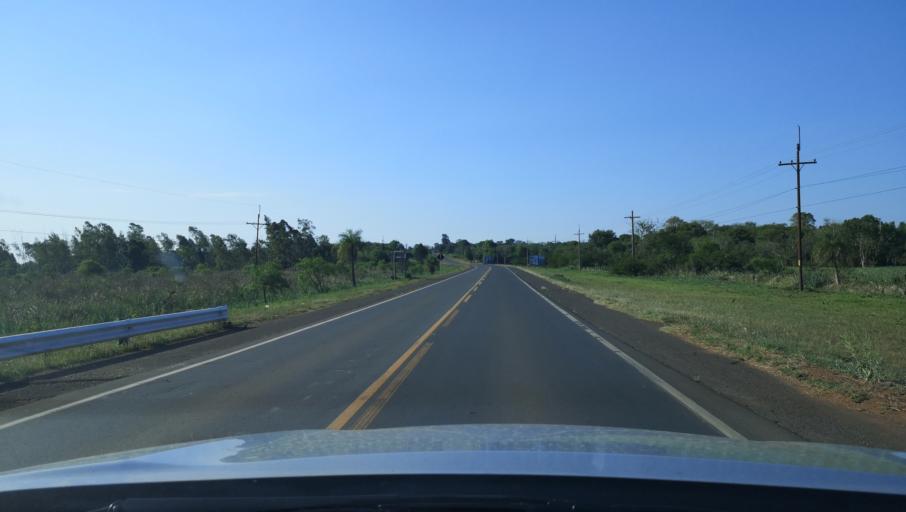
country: PY
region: Misiones
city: Santa Maria
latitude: -26.8703
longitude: -57.0326
